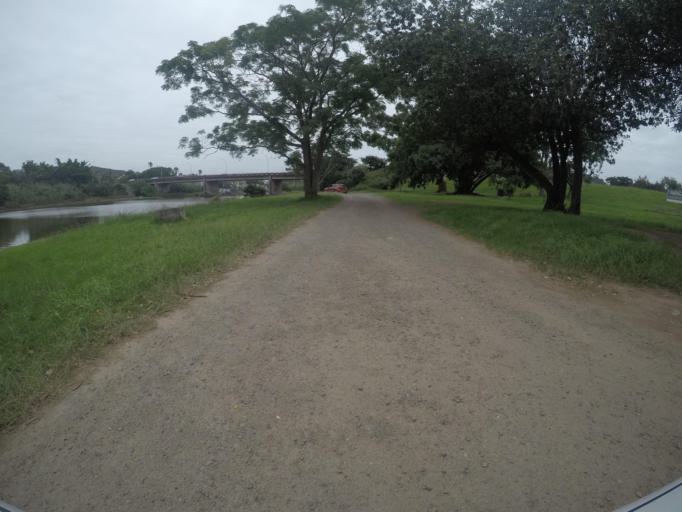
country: ZA
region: Eastern Cape
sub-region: Buffalo City Metropolitan Municipality
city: East London
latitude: -32.9748
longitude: 27.9266
